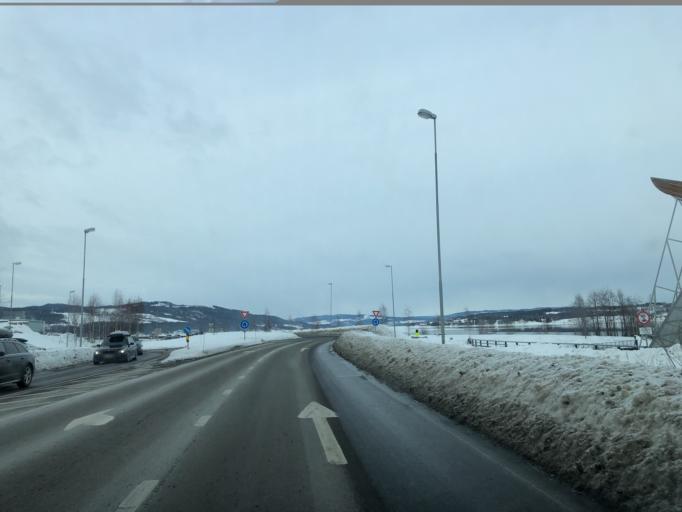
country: NO
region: Oppland
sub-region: Gjovik
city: Gjovik
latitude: 60.7976
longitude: 10.6963
